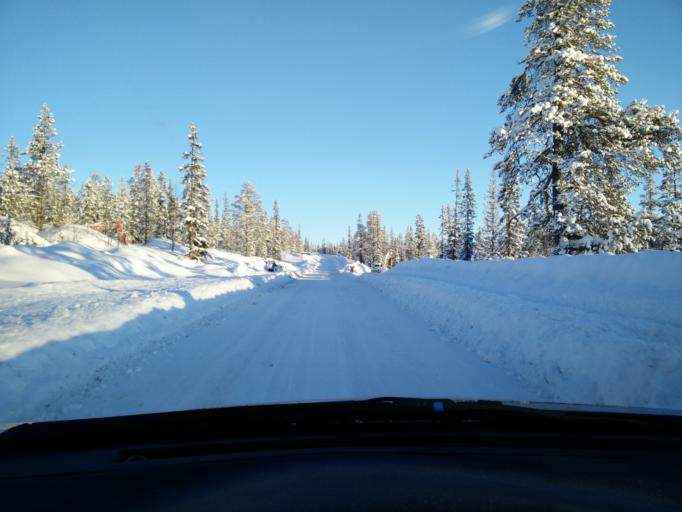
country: SE
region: Jaemtland
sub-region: Bergs Kommun
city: Hoverberg
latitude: 62.4980
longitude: 14.1169
